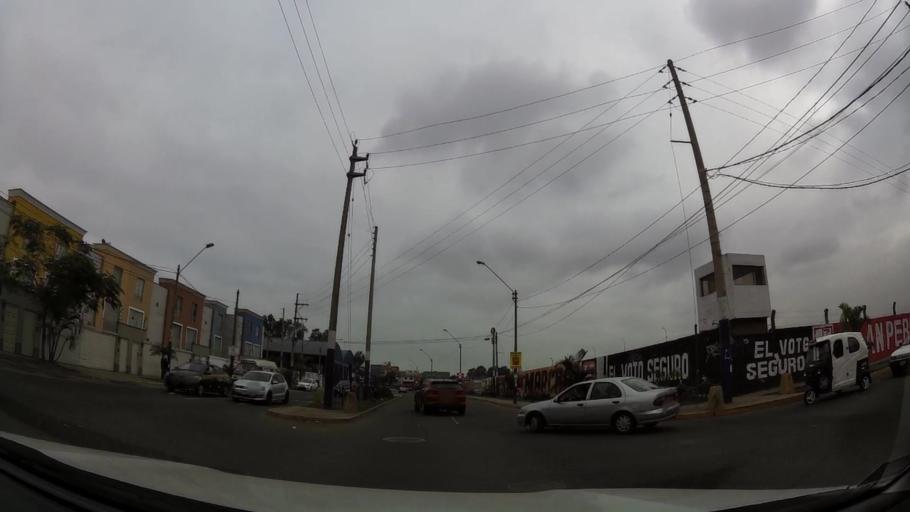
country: PE
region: Lima
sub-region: Lima
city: Surco
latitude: -12.1741
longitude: -77.0024
